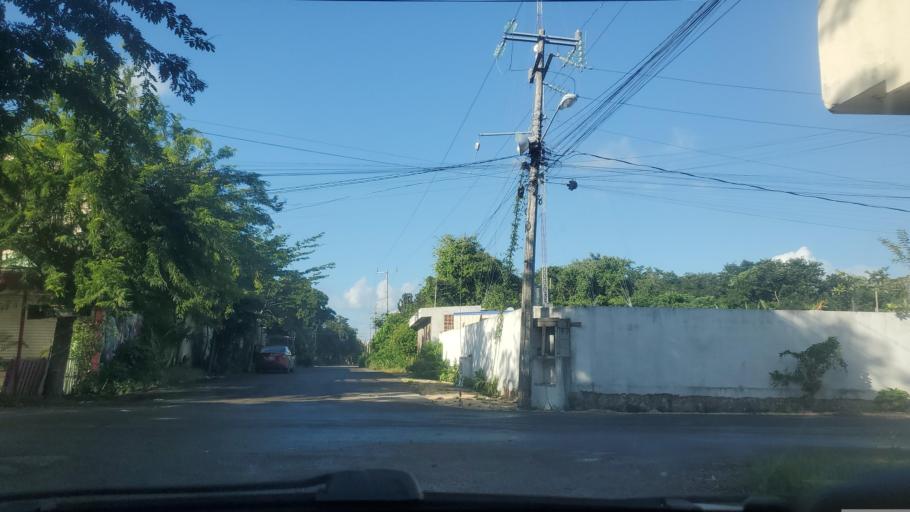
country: MX
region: Quintana Roo
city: Tulum
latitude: 20.2088
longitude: -87.4740
